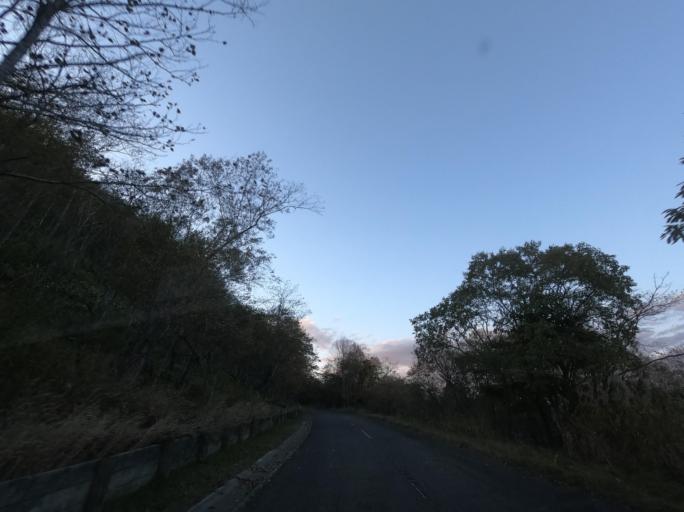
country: JP
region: Hokkaido
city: Kushiro
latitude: 43.1917
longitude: 144.4660
